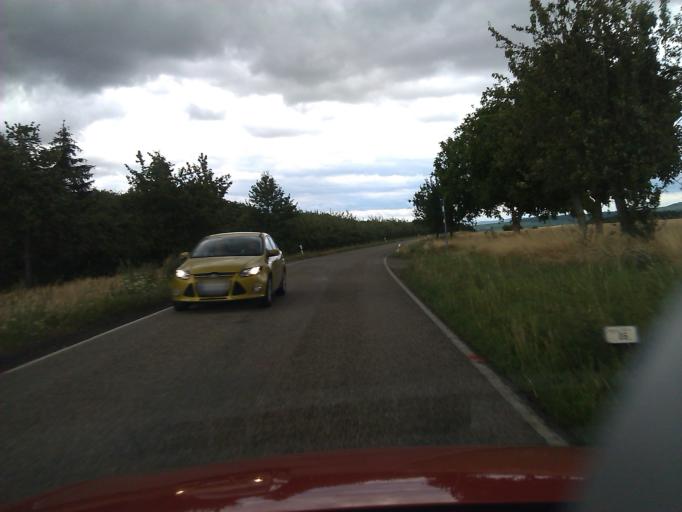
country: DE
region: Baden-Wuerttemberg
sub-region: Regierungsbezirk Stuttgart
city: Guglingen
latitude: 49.0879
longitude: 8.9903
